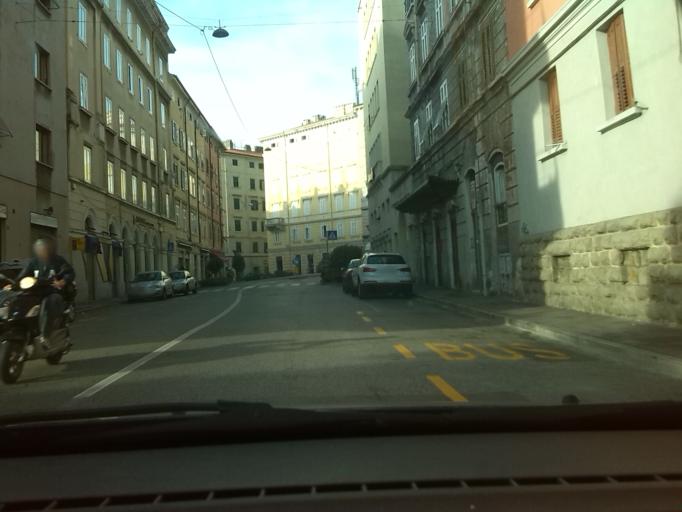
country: IT
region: Friuli Venezia Giulia
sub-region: Provincia di Trieste
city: Trieste
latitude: 45.6411
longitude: 13.7813
